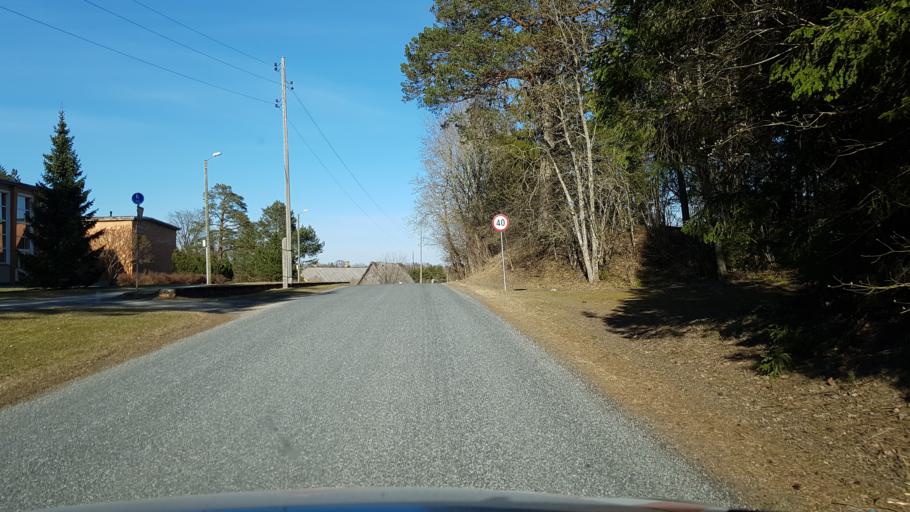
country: EE
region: Laeaene-Virumaa
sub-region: Vinni vald
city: Vinni
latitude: 59.1658
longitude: 26.5902
